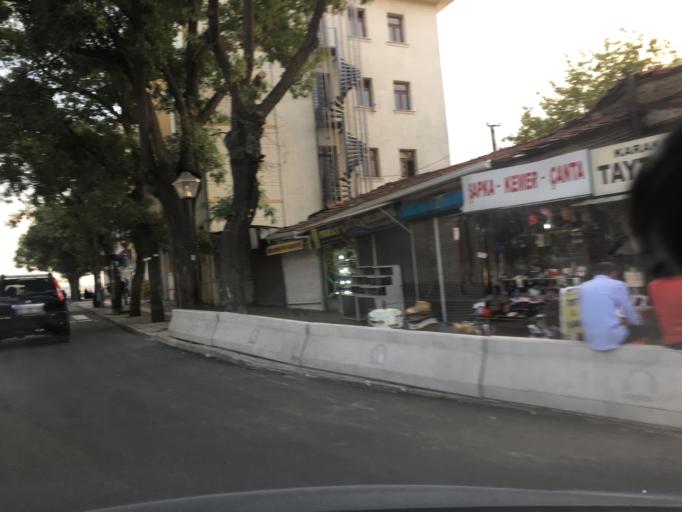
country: TR
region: Ankara
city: Ankara
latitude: 39.9352
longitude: 32.8619
